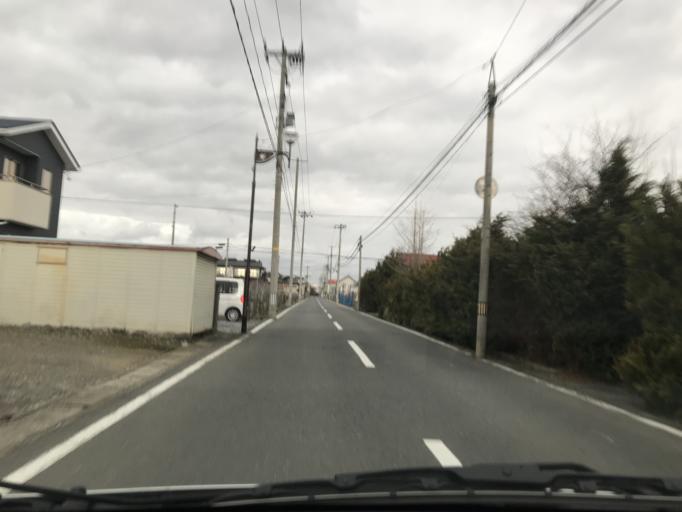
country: JP
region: Iwate
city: Mizusawa
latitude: 39.1334
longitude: 141.1605
